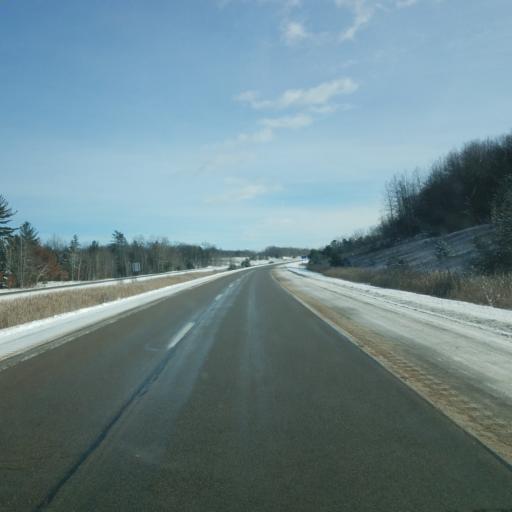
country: US
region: Michigan
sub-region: Clare County
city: Clare
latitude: 43.8705
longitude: -84.8863
